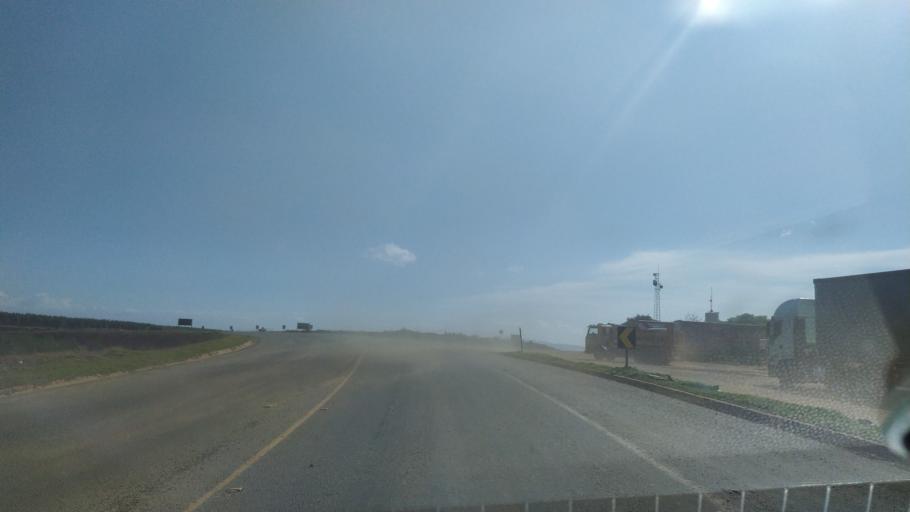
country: BR
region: Parana
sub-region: Telemaco Borba
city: Telemaco Borba
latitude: -24.2388
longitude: -50.7595
